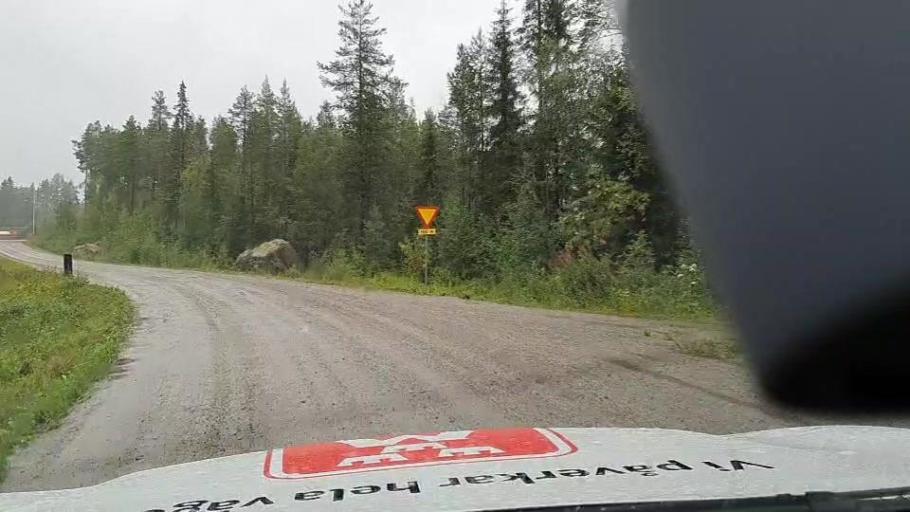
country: SE
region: Jaemtland
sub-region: OEstersunds Kommun
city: Brunflo
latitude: 62.8459
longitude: 15.0251
